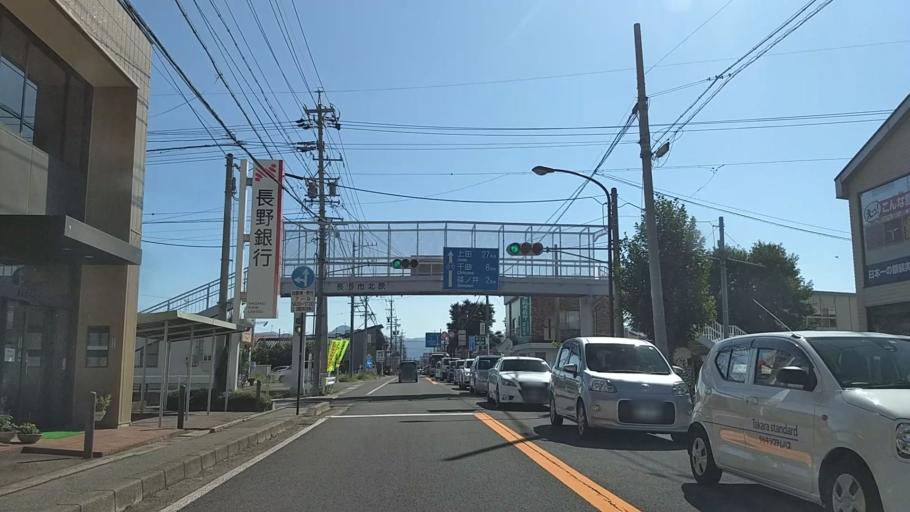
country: JP
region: Nagano
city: Nagano-shi
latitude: 36.5922
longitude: 138.1551
